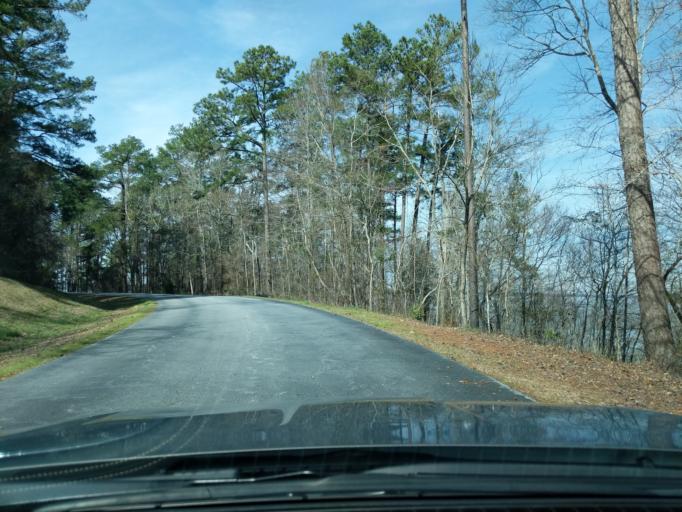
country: US
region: Georgia
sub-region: Columbia County
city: Evans
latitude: 33.6643
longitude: -82.1891
